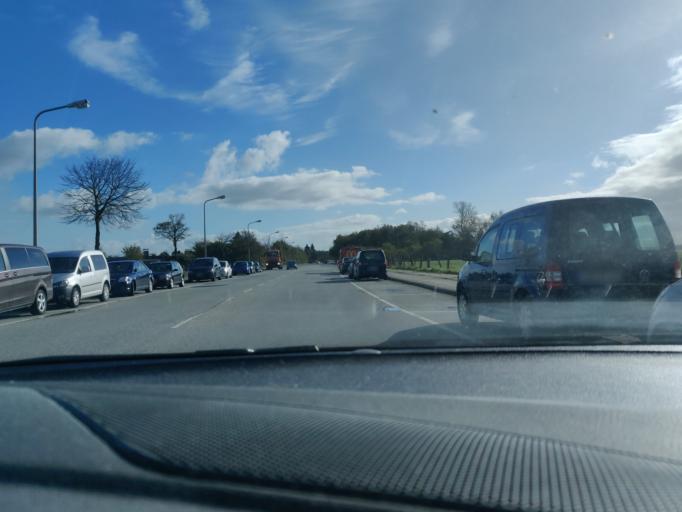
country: DE
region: Lower Saxony
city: Cuxhaven
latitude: 53.8803
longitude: 8.6734
